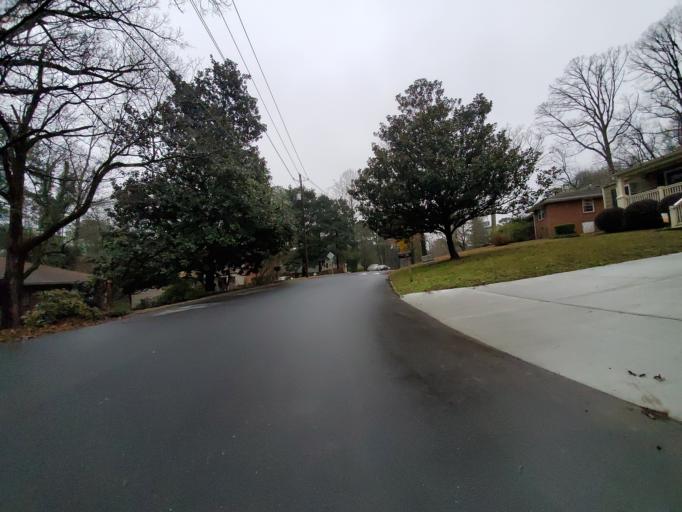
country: US
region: Georgia
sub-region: DeKalb County
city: North Decatur
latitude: 33.7951
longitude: -84.3037
